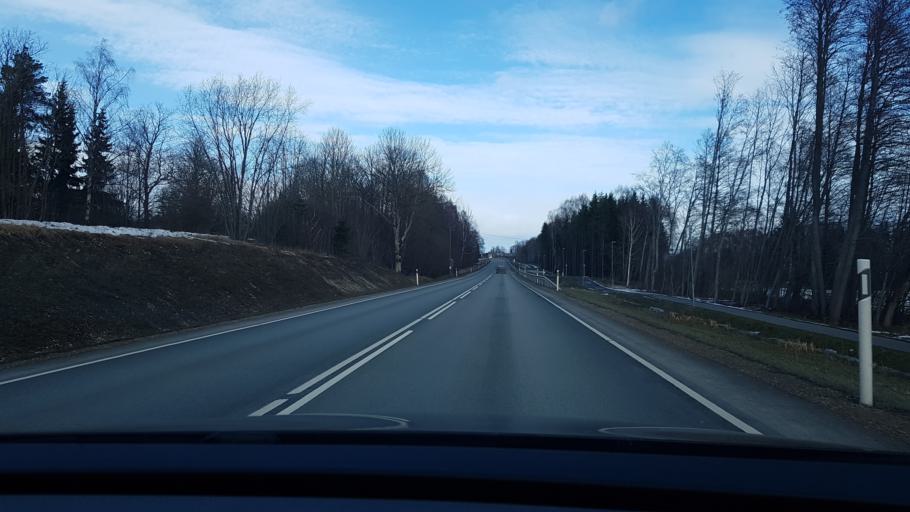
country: EE
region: Paernumaa
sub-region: Tootsi vald
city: Tootsi
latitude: 58.5108
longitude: 24.8101
